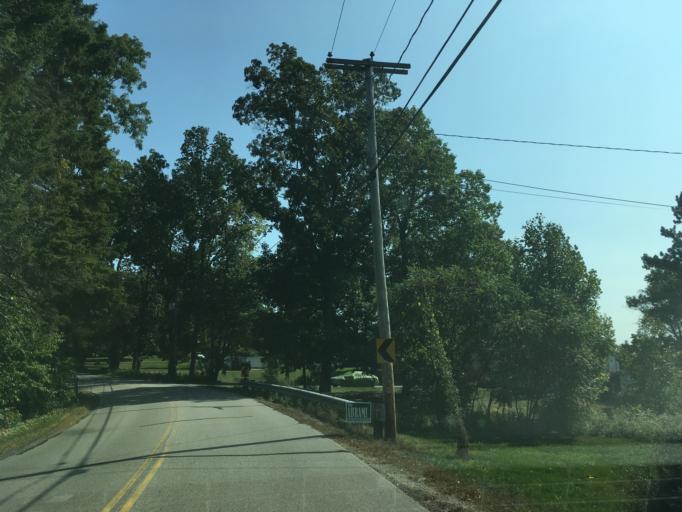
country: US
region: New Hampshire
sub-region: Rockingham County
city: Exeter
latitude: 43.0026
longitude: -70.9134
